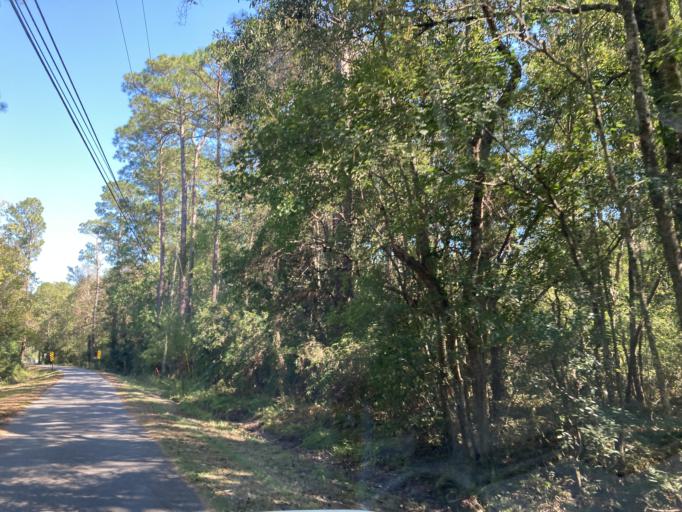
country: US
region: Mississippi
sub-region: Jackson County
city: Gulf Hills
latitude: 30.4612
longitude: -88.8399
